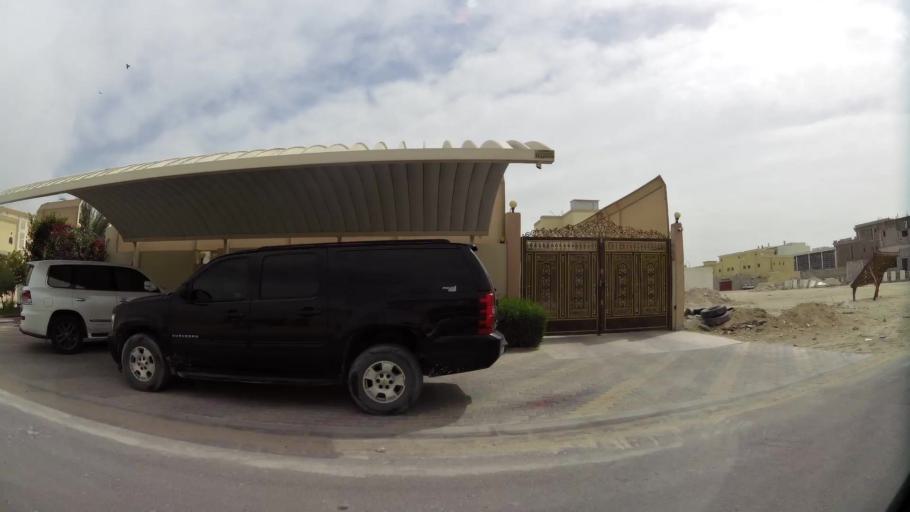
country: QA
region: Al Wakrah
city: Al Wukayr
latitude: 25.1973
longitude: 51.4589
